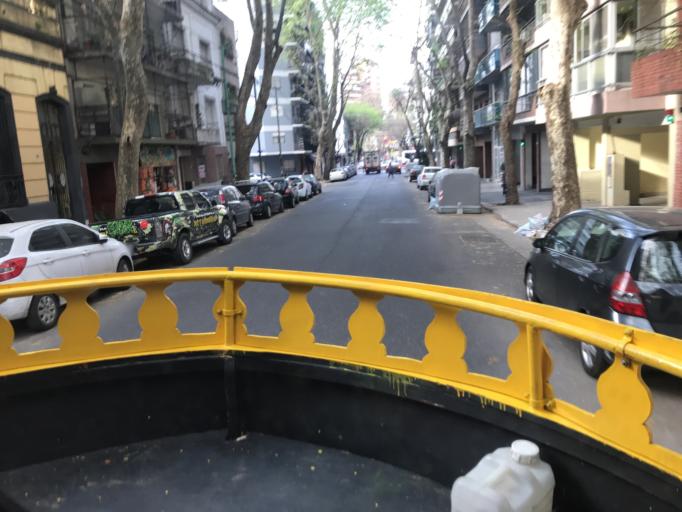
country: AR
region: Buenos Aires F.D.
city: Retiro
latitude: -34.5913
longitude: -58.4177
